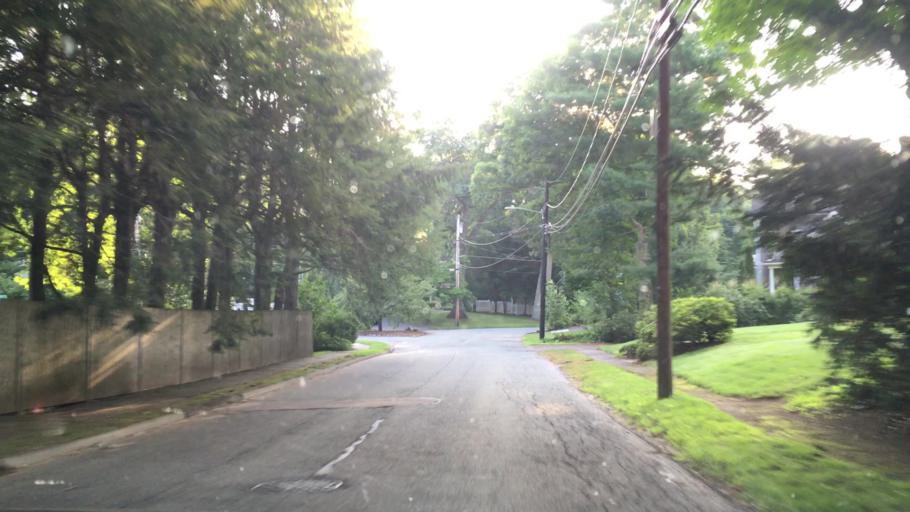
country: US
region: Massachusetts
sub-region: Norfolk County
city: Wellesley
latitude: 42.3099
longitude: -71.2890
